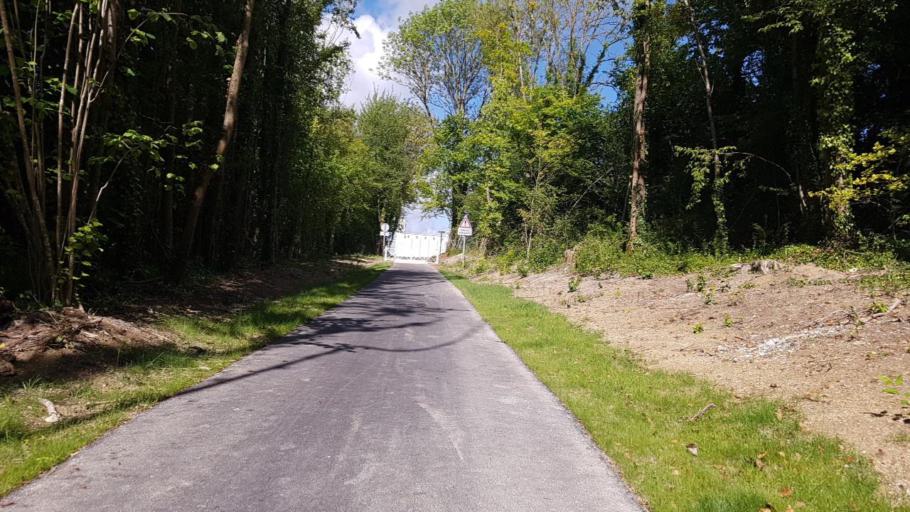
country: FR
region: Champagne-Ardenne
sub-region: Departement de la Marne
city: Tours-sur-Marne
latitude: 49.0447
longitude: 4.1056
